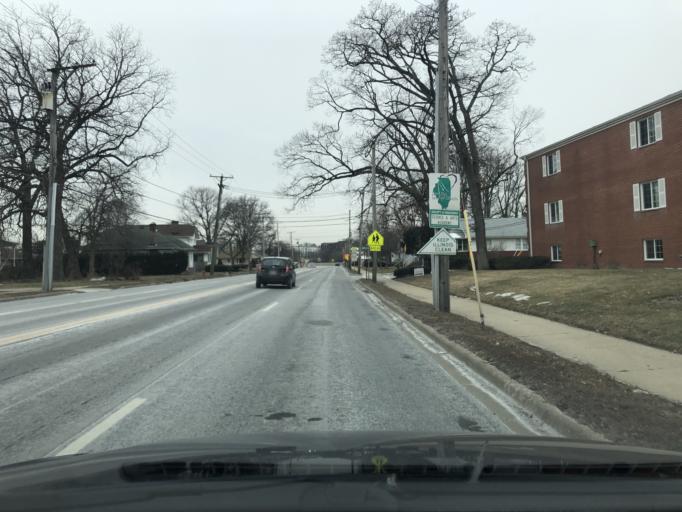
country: US
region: Illinois
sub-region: Cook County
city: Des Plaines
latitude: 42.0391
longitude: -87.8747
